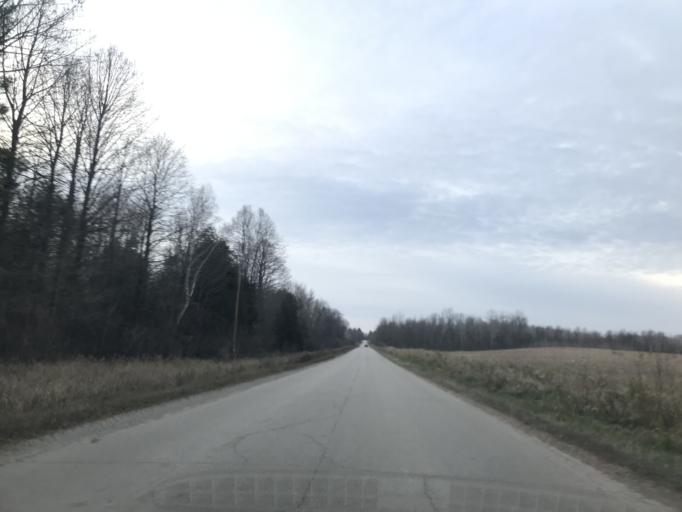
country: US
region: Wisconsin
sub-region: Marinette County
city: Peshtigo
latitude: 45.0770
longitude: -87.7996
